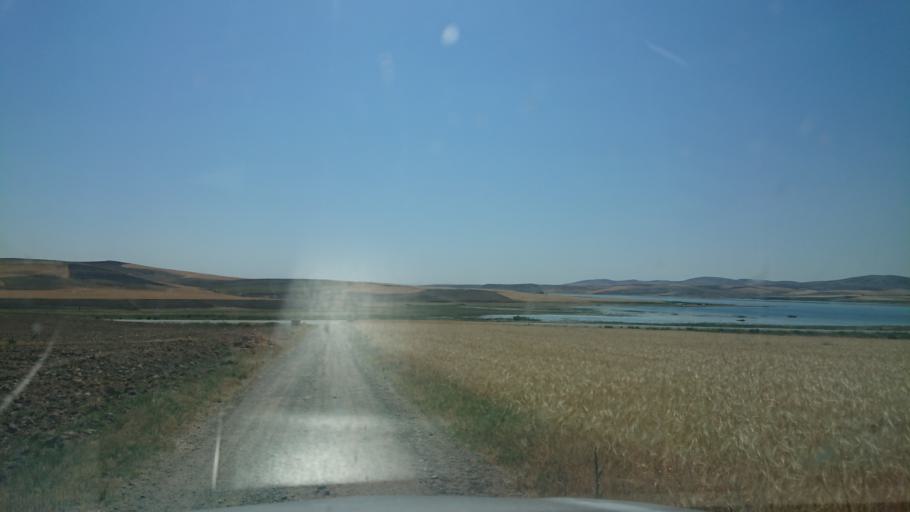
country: TR
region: Aksaray
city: Sariyahsi
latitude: 39.0552
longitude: 33.8965
